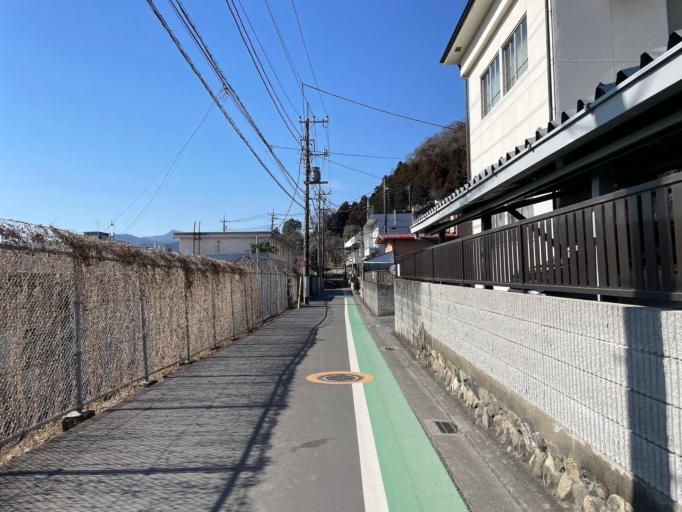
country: JP
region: Tokyo
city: Ome
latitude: 35.7909
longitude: 139.2577
